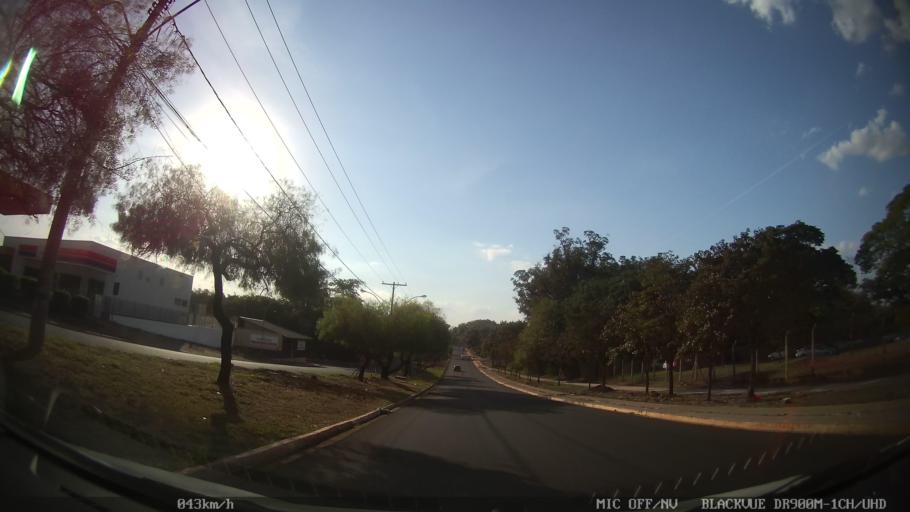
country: BR
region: Sao Paulo
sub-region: Ribeirao Preto
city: Ribeirao Preto
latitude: -21.1464
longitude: -47.8314
